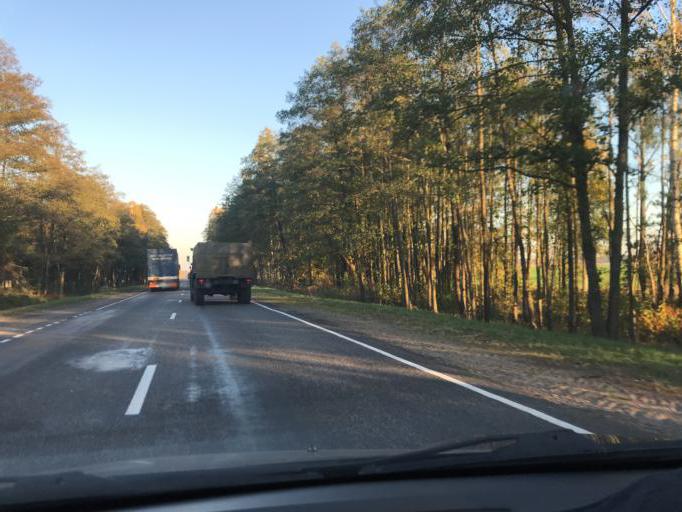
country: BY
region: Minsk
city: Staryya Darohi
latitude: 53.0475
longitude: 28.0915
